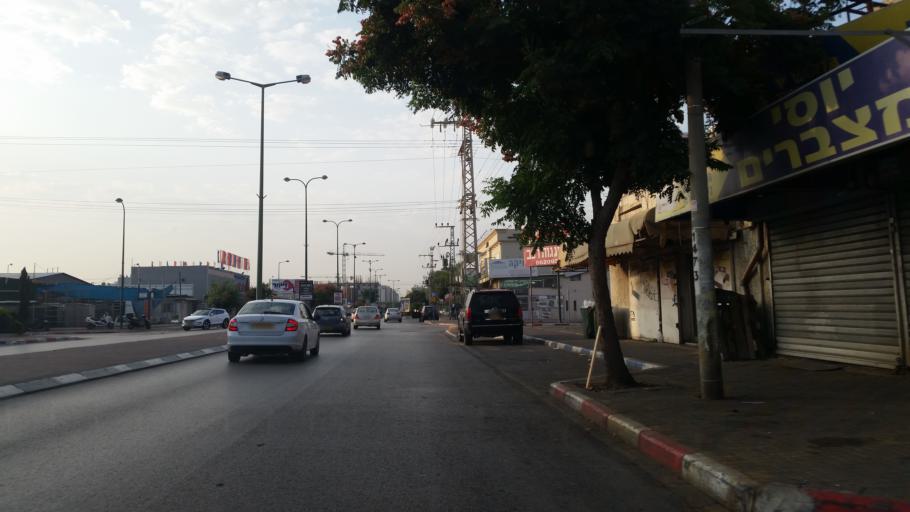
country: IL
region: Central District
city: Bet Yizhaq
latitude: 32.3191
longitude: 34.8741
